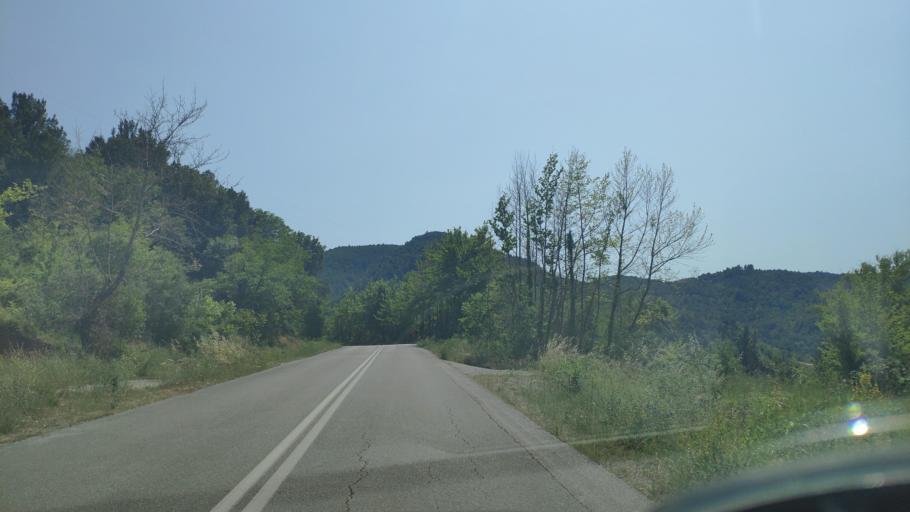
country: GR
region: Epirus
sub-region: Nomos Artas
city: Ano Kalentini
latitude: 39.2295
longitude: 21.1546
